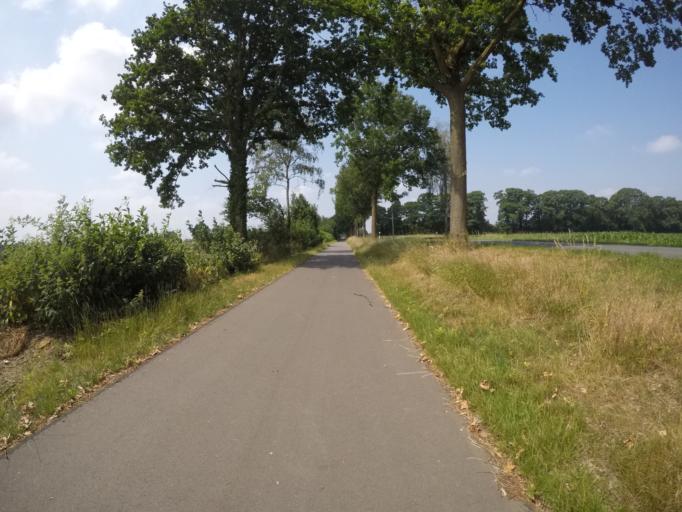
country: DE
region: North Rhine-Westphalia
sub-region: Regierungsbezirk Dusseldorf
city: Bocholt
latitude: 51.8436
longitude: 6.5436
